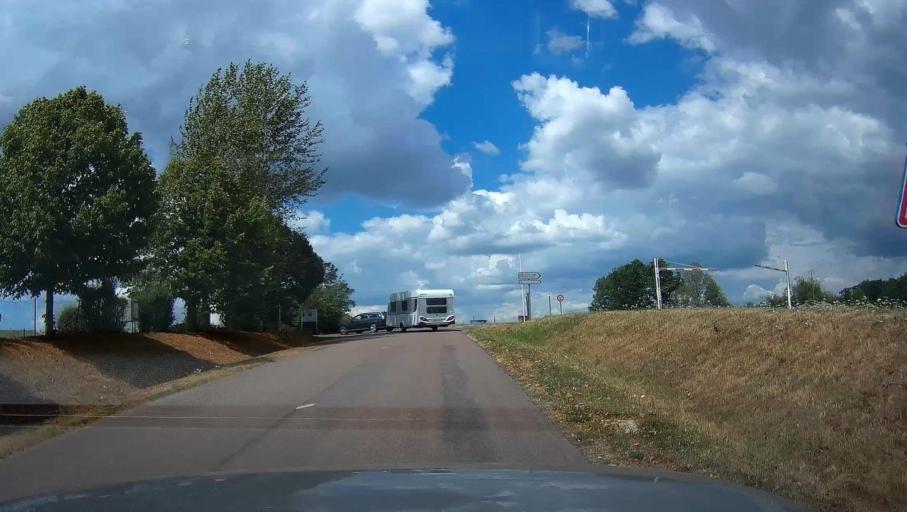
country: FR
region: Champagne-Ardenne
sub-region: Departement de la Haute-Marne
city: Langres
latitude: 47.8726
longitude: 5.3812
